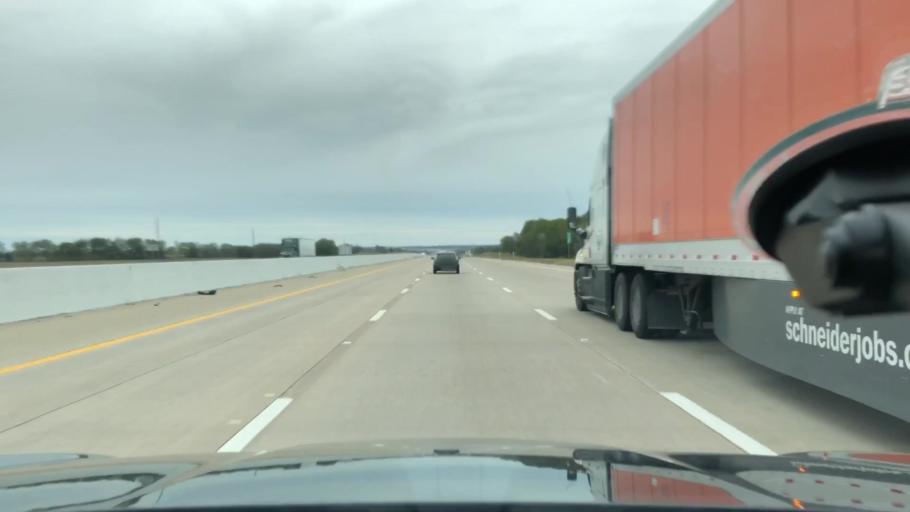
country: US
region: Texas
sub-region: Ellis County
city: Italy
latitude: 32.2034
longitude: -96.8956
